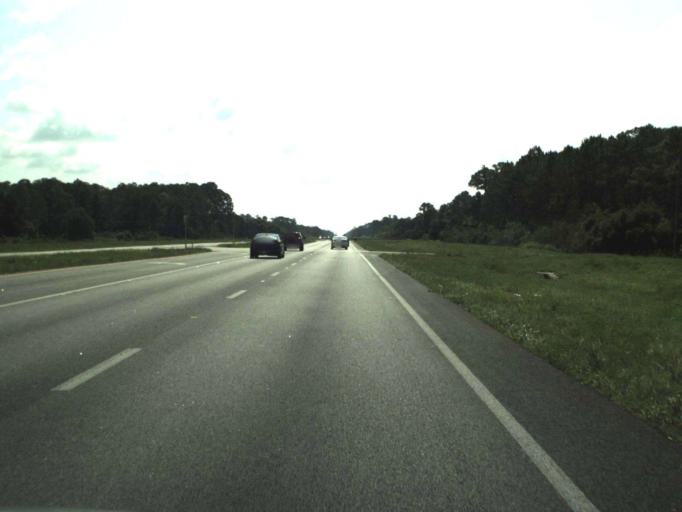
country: US
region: Florida
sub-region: Volusia County
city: Samsula-Spruce Creek
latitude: 29.0113
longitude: -81.0594
